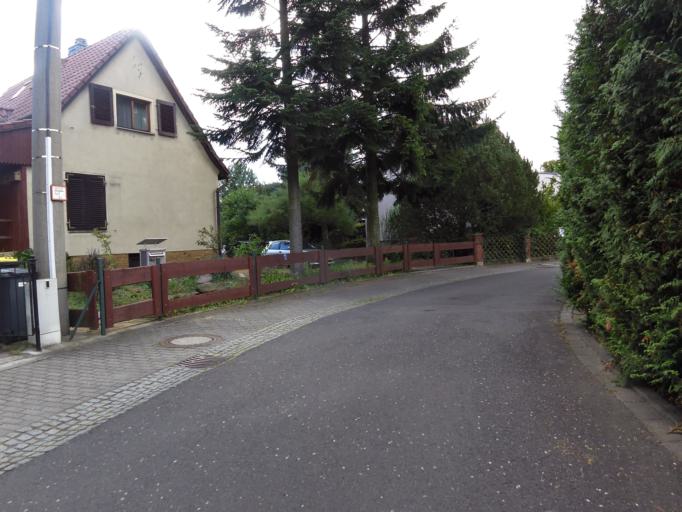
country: DE
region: Saxony
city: Leipzig
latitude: 51.3881
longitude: 12.3523
